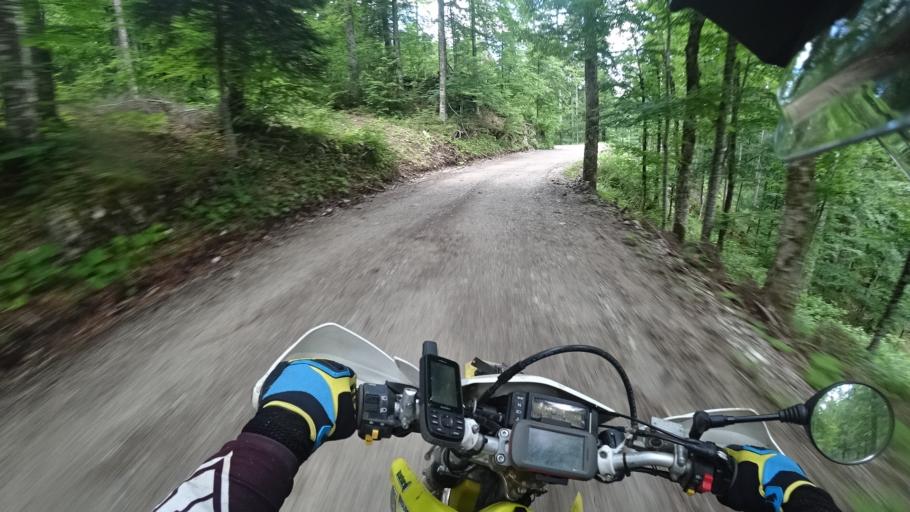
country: SI
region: Osilnica
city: Osilnica
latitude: 45.5112
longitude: 14.6126
